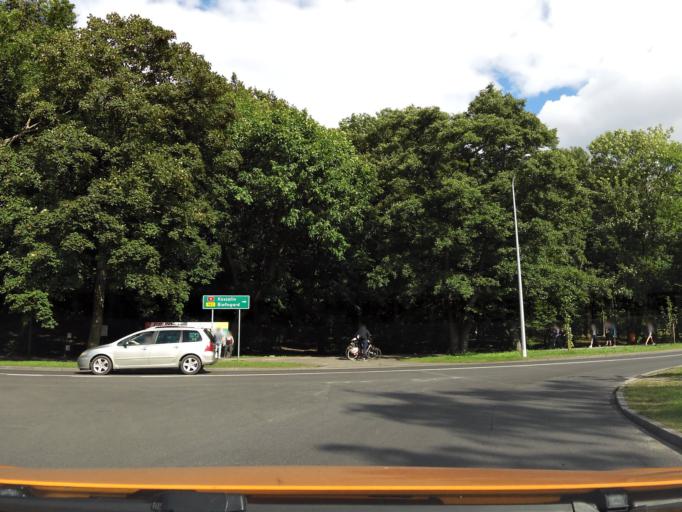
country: PL
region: West Pomeranian Voivodeship
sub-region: Powiat kolobrzeski
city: Kolobrzeg
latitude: 54.1842
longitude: 15.5921
